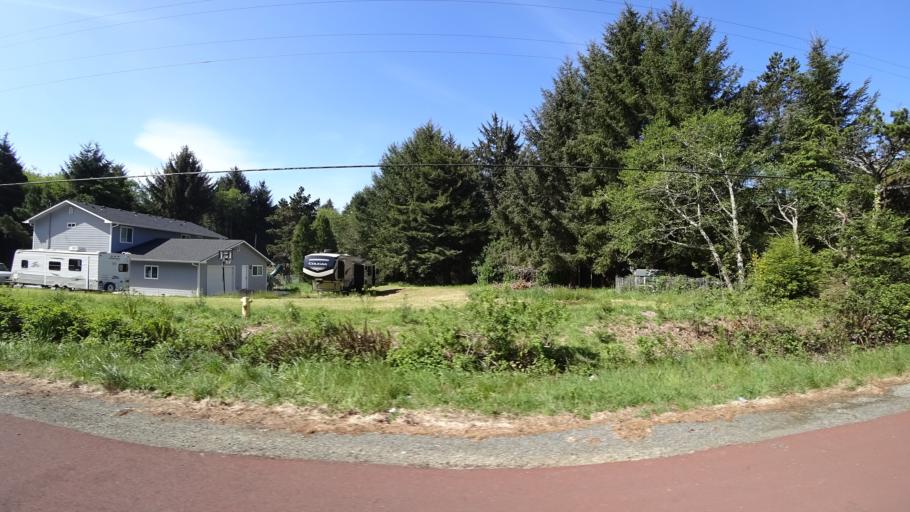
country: US
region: Oregon
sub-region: Curry County
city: Harbor
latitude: 41.9497
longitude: -124.1999
